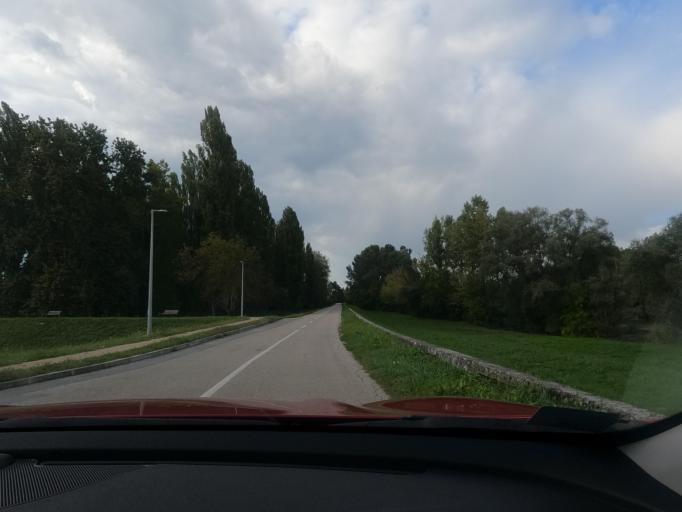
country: HR
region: Sisacko-Moslavacka
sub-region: Grad Sisak
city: Sisak
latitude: 45.4726
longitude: 16.3855
